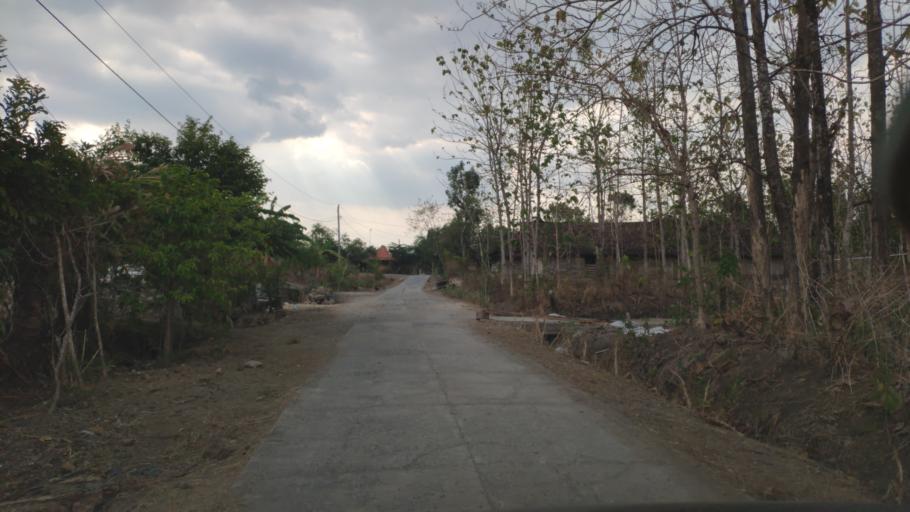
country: ID
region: Central Java
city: Randublatung
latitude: -7.2903
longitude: 111.3132
